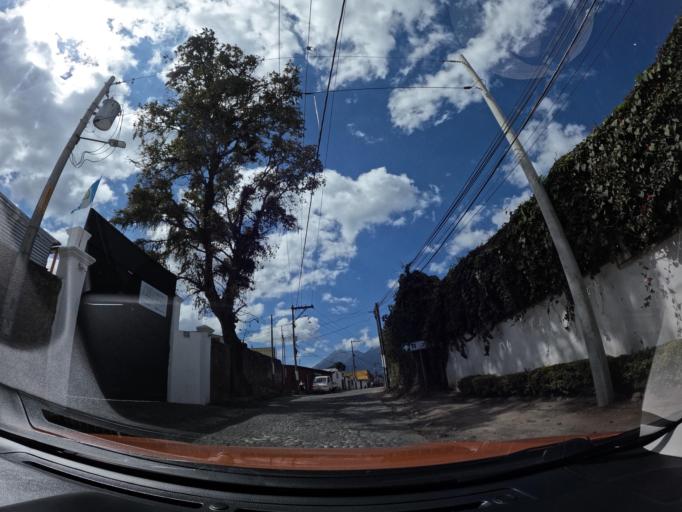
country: GT
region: Sacatepequez
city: Ciudad Vieja
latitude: 14.5269
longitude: -90.7478
